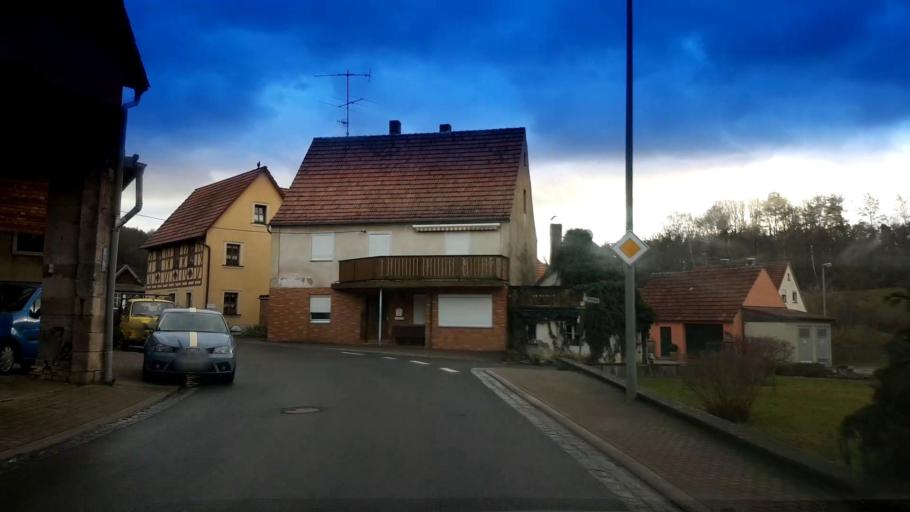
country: DE
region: Bavaria
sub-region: Regierungsbezirk Unterfranken
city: Stettfeld
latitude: 50.0004
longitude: 10.7452
